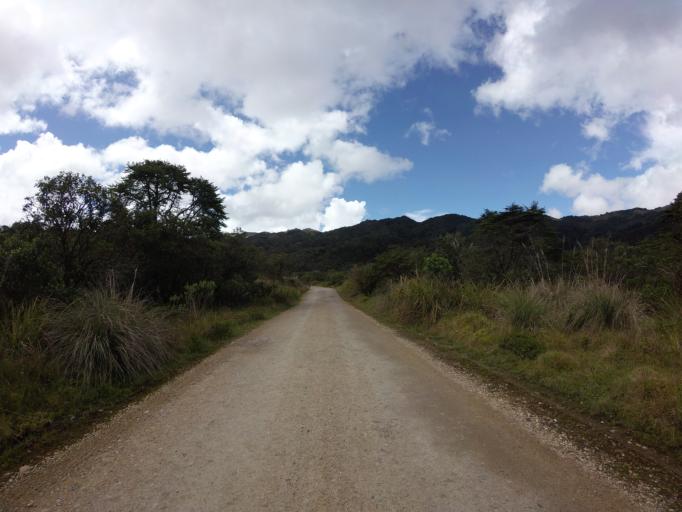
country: CO
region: Cundinamarca
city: Junin
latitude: 4.6265
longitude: -73.7228
